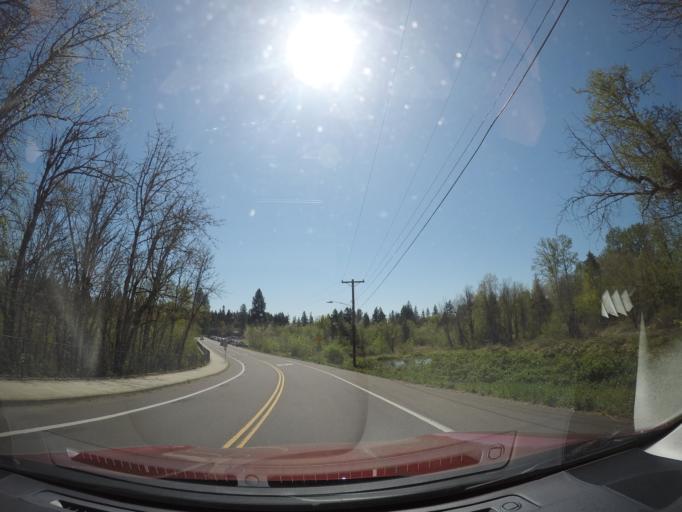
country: US
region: Oregon
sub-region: Washington County
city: Tualatin
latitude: 45.3994
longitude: -122.7722
